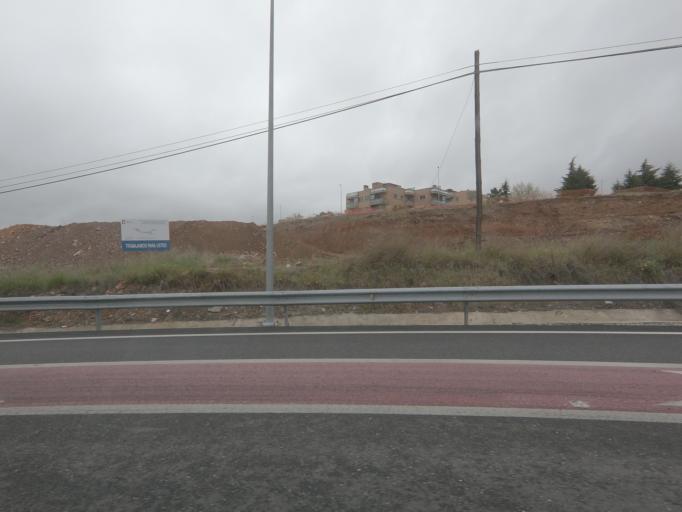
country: ES
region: Extremadura
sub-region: Provincia de Caceres
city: Caceres
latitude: 39.4678
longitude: -6.4002
